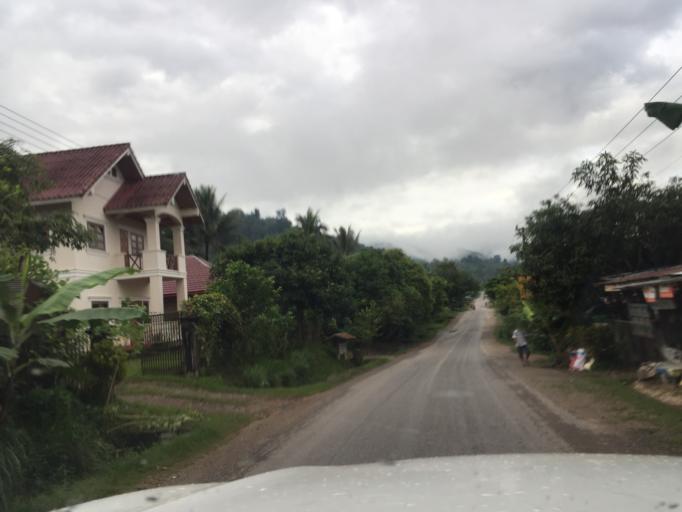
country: LA
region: Oudomxai
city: Muang La
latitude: 20.8656
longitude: 102.1166
